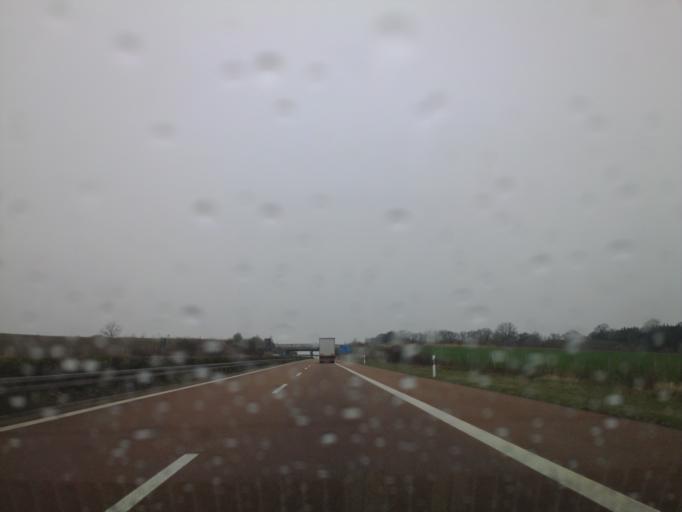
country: DE
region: Mecklenburg-Vorpommern
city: Tessin
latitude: 54.0337
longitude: 12.3982
